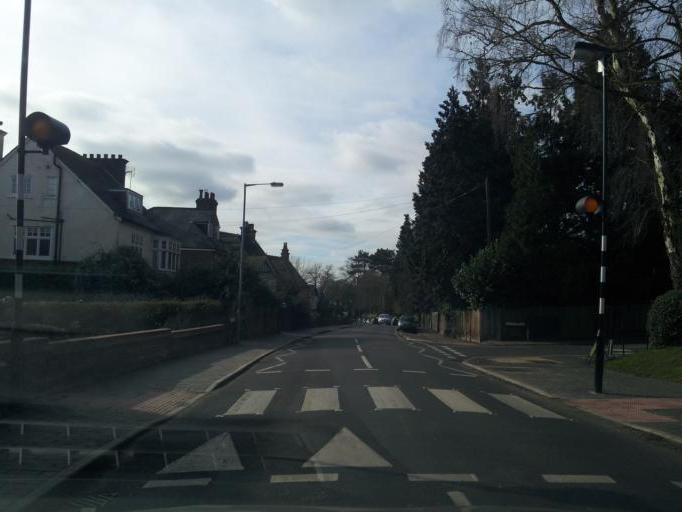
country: GB
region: England
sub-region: Hertfordshire
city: St Albans
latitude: 51.7575
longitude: -0.3253
